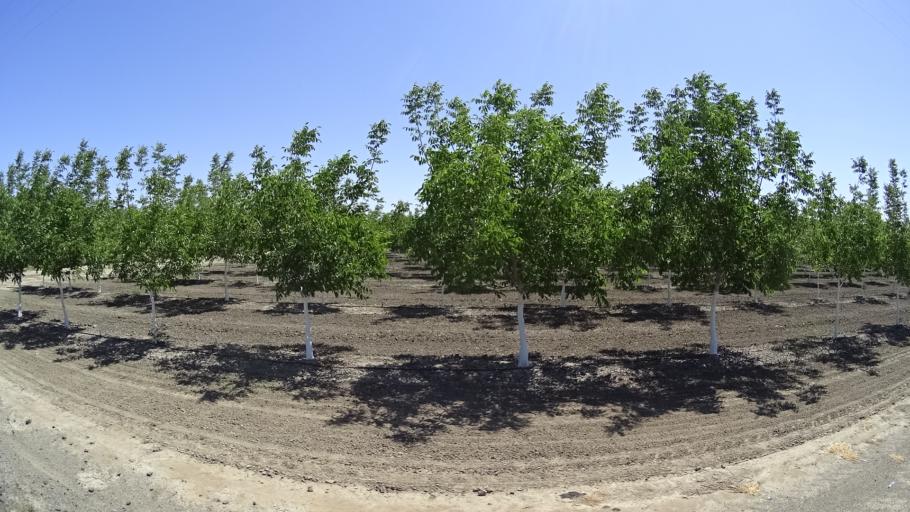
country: US
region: California
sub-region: Kings County
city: Armona
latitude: 36.2470
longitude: -119.7268
